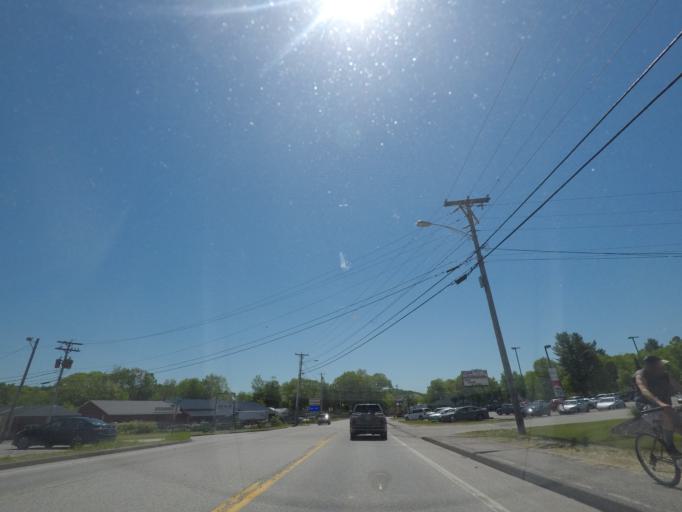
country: US
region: Maine
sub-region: Kennebec County
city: Farmingdale
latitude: 44.2582
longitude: -69.7752
